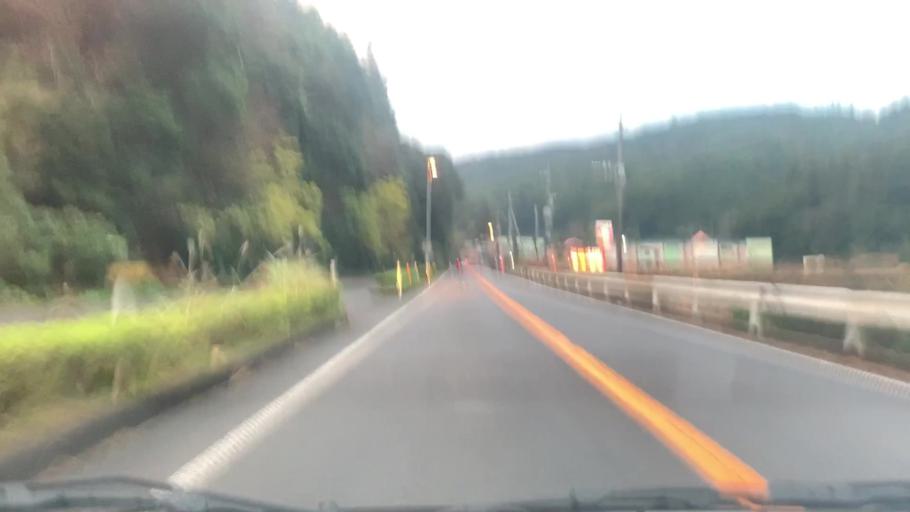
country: JP
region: Saga Prefecture
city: Ureshinomachi-shimojuku
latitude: 33.0661
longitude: 129.9617
